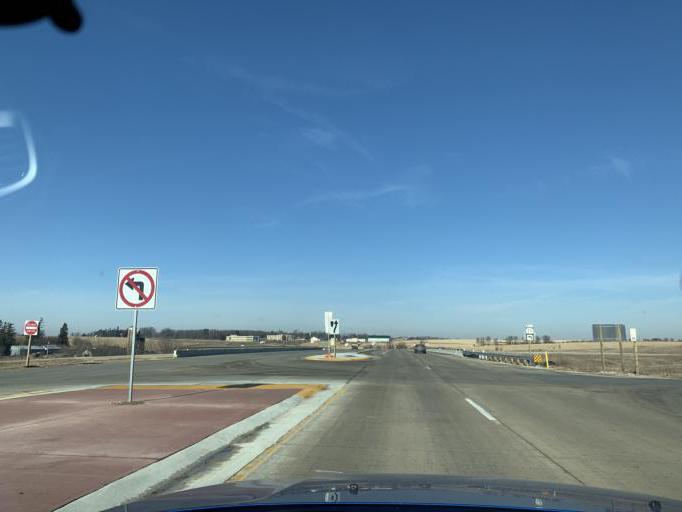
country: US
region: Wisconsin
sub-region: Green County
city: Monroe
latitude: 42.6126
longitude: -89.6523
